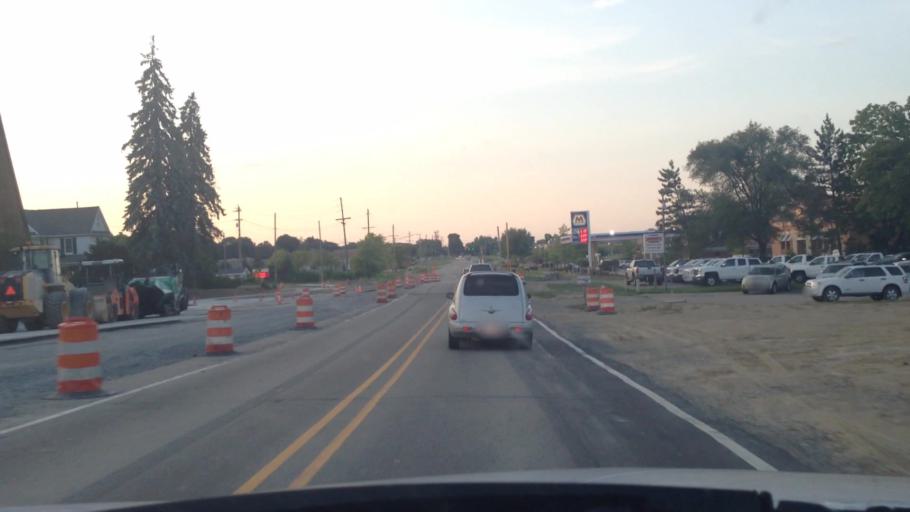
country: US
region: Michigan
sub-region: Oakland County
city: Auburn Hills
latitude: 42.7223
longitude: -83.3074
